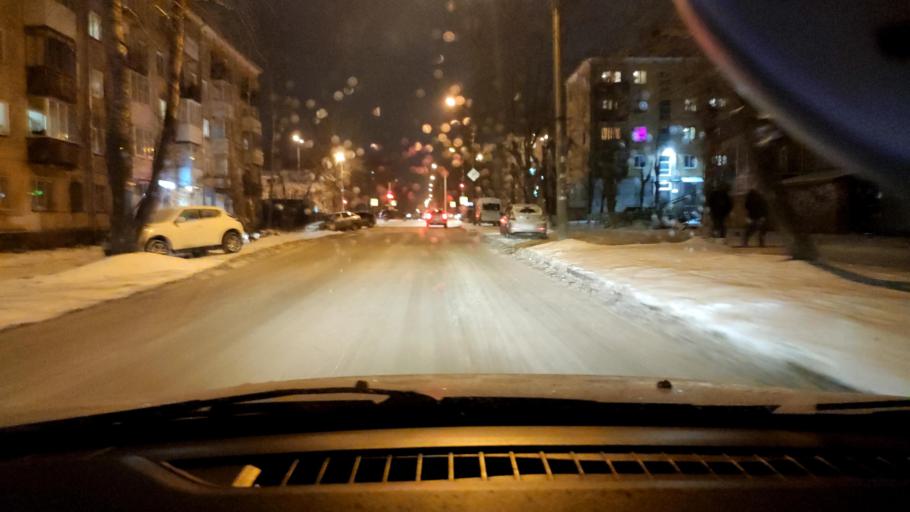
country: RU
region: Perm
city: Kultayevo
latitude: 58.0032
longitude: 55.9505
